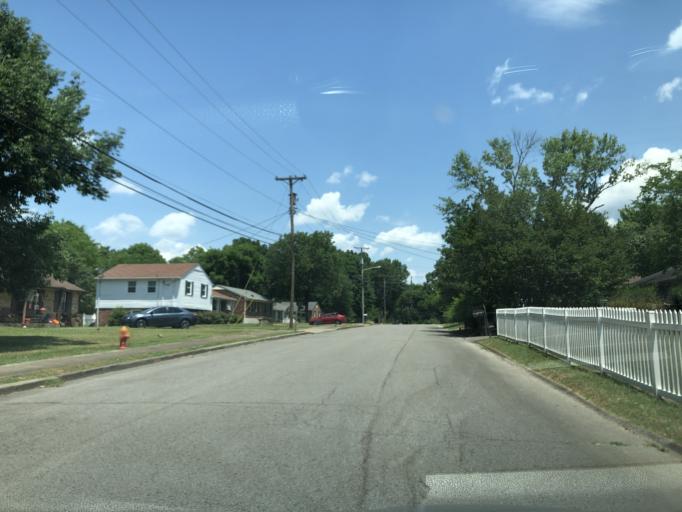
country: US
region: Tennessee
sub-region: Davidson County
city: Goodlettsville
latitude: 36.2712
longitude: -86.7012
